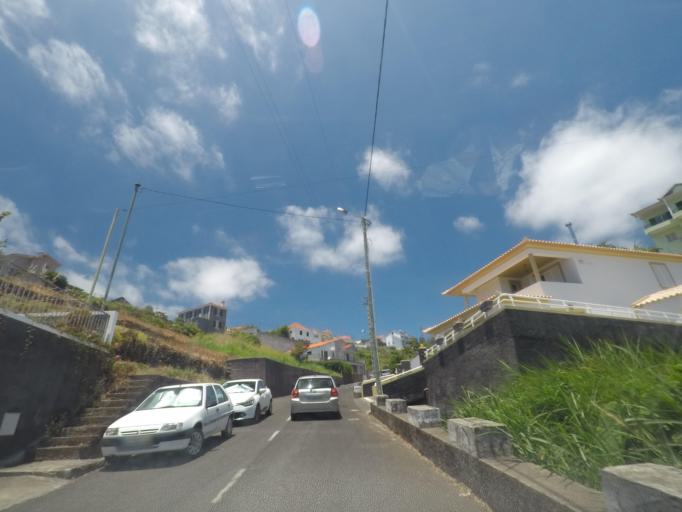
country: PT
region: Madeira
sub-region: Calheta
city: Estreito da Calheta
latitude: 32.7353
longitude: -17.1727
